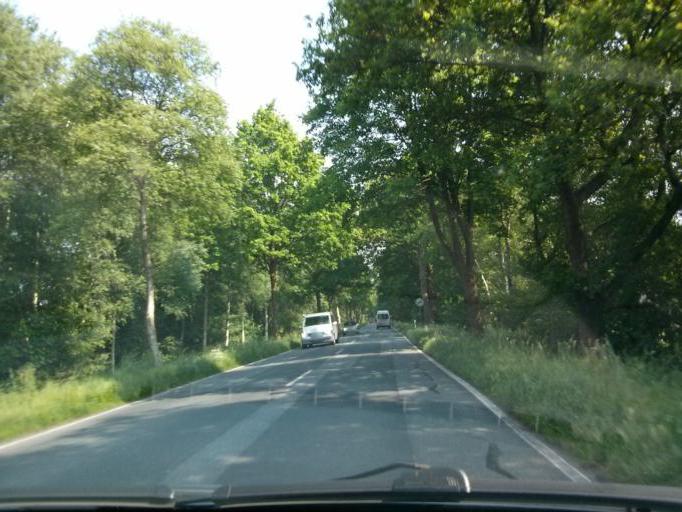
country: DE
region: Lower Saxony
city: Schiffdorf
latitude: 53.5202
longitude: 8.6724
